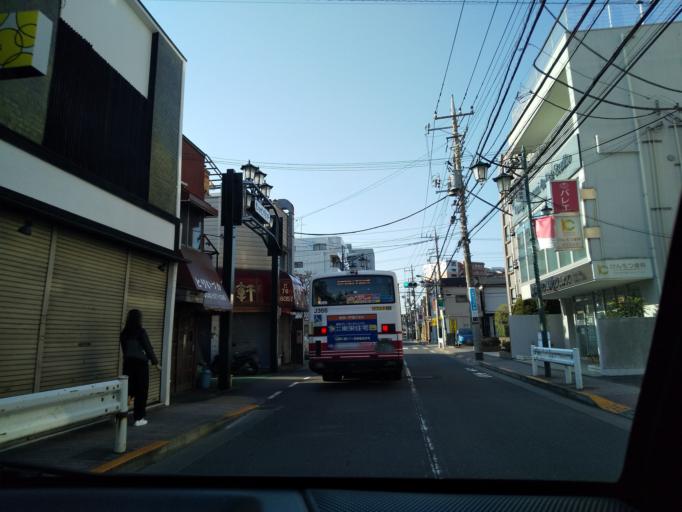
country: JP
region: Tokyo
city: Kokubunji
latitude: 35.7024
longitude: 139.4465
